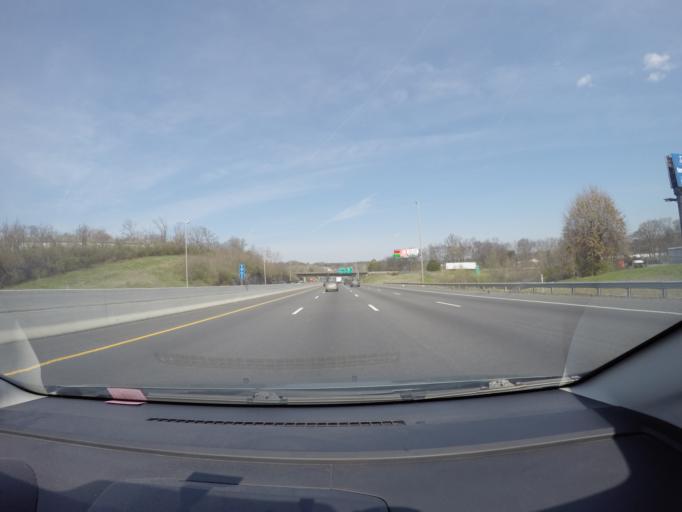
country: US
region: Tennessee
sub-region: Davidson County
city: Oak Hill
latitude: 36.0947
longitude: -86.7068
